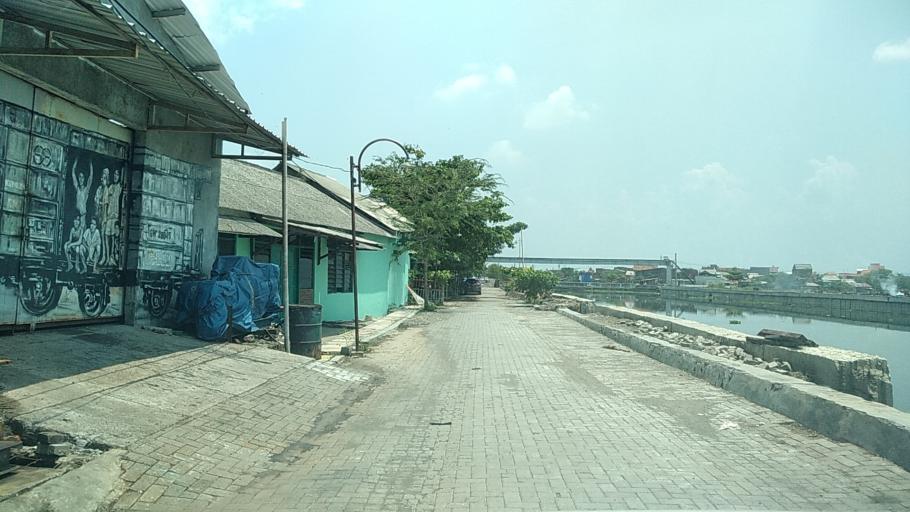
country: ID
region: Central Java
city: Semarang
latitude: -6.9542
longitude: 110.4383
